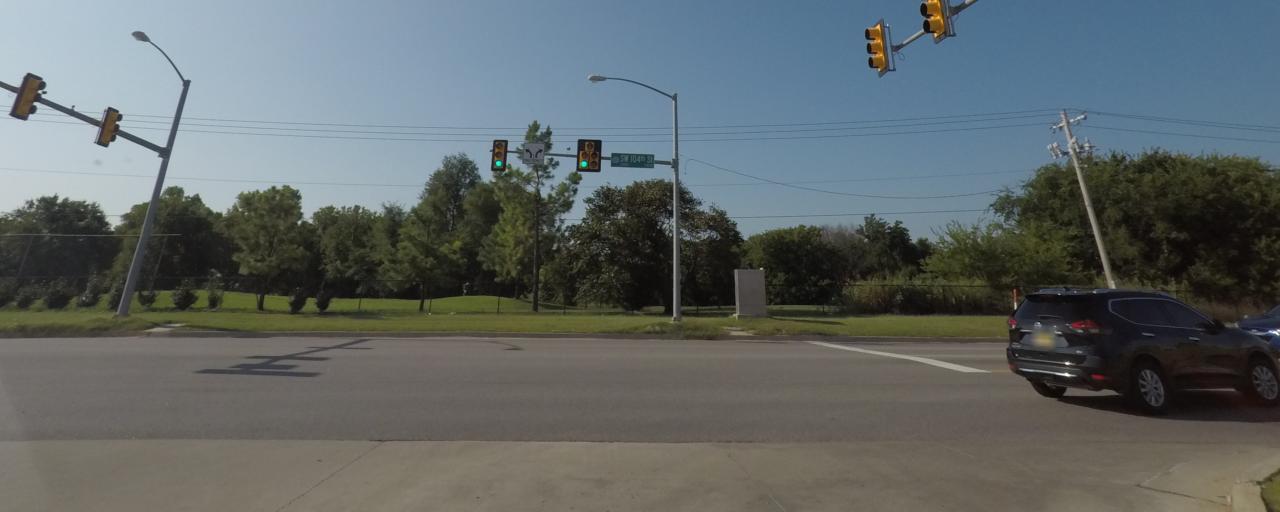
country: US
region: Oklahoma
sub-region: Cleveland County
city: Moore
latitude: 35.3633
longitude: -97.5779
